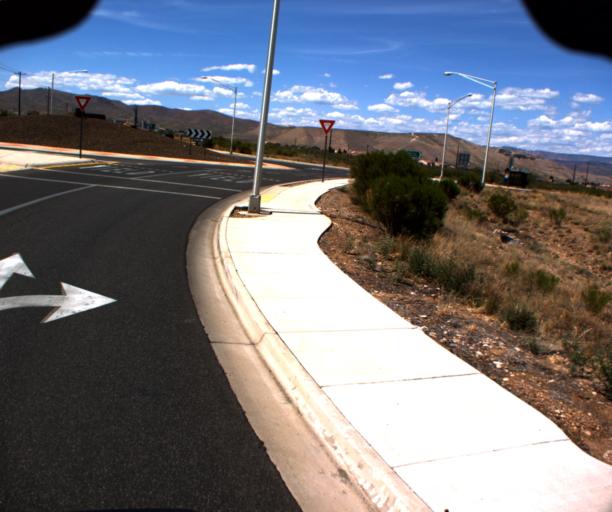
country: US
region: Arizona
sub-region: Yavapai County
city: Clarkdale
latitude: 34.7582
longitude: -112.0583
